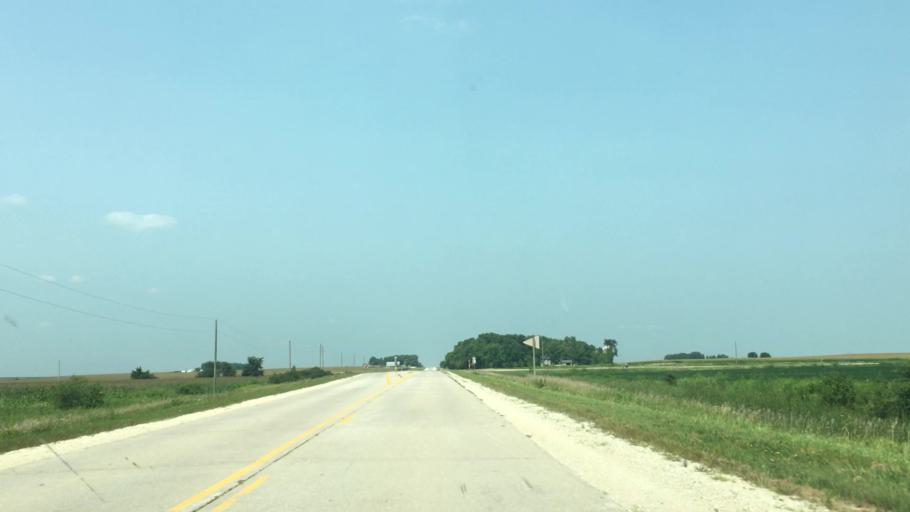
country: US
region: Iowa
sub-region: Fayette County
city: Fayette
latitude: 42.7573
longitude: -91.8043
